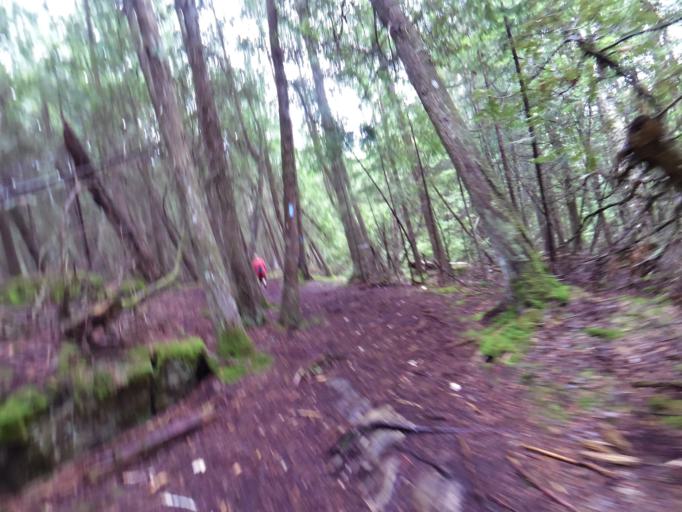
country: CA
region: Ontario
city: Tobermory
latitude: 45.2619
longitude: -81.6439
